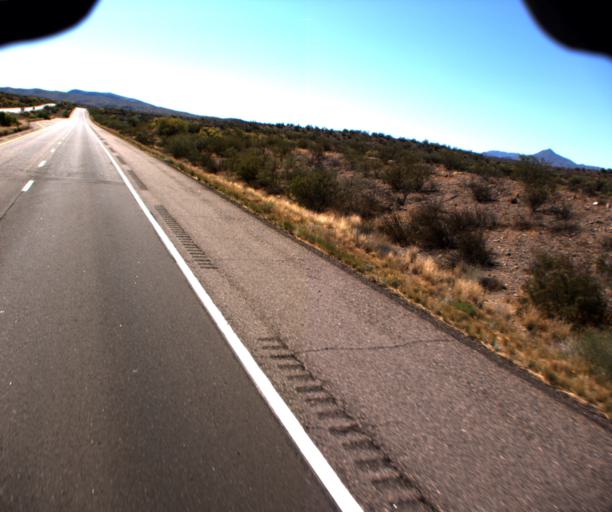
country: US
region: Arizona
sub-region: Yavapai County
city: Bagdad
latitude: 34.6339
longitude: -113.5516
